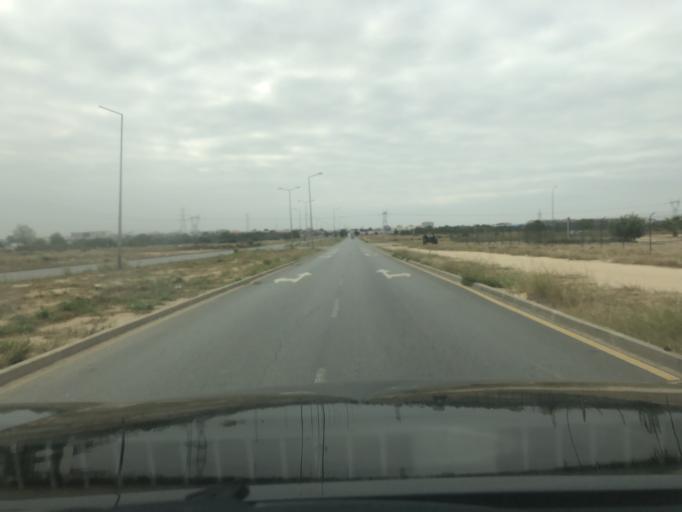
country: AO
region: Luanda
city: Luanda
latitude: -8.9759
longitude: 13.2836
